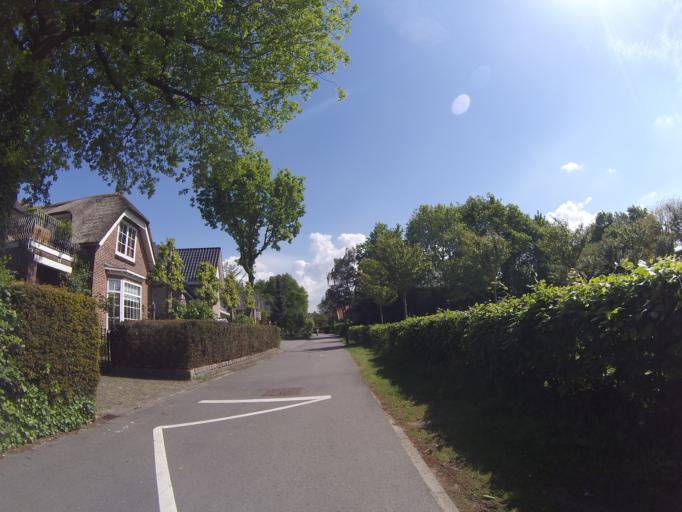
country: NL
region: Utrecht
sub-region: Gemeente Soest
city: Soest
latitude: 52.1781
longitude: 5.3082
